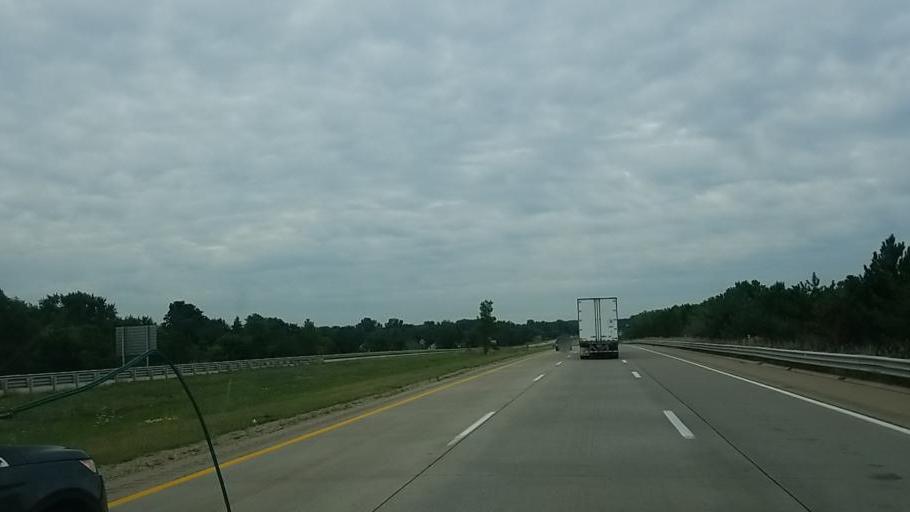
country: US
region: Michigan
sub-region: Branch County
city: Coldwater
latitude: 41.9324
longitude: -84.9733
